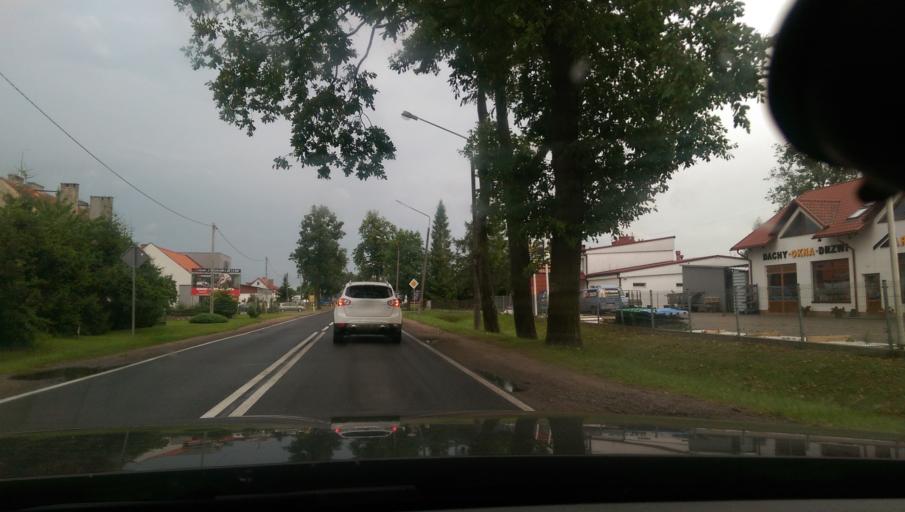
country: PL
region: Warmian-Masurian Voivodeship
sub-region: Powiat szczycienski
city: Szczytno
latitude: 53.5546
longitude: 20.9876
